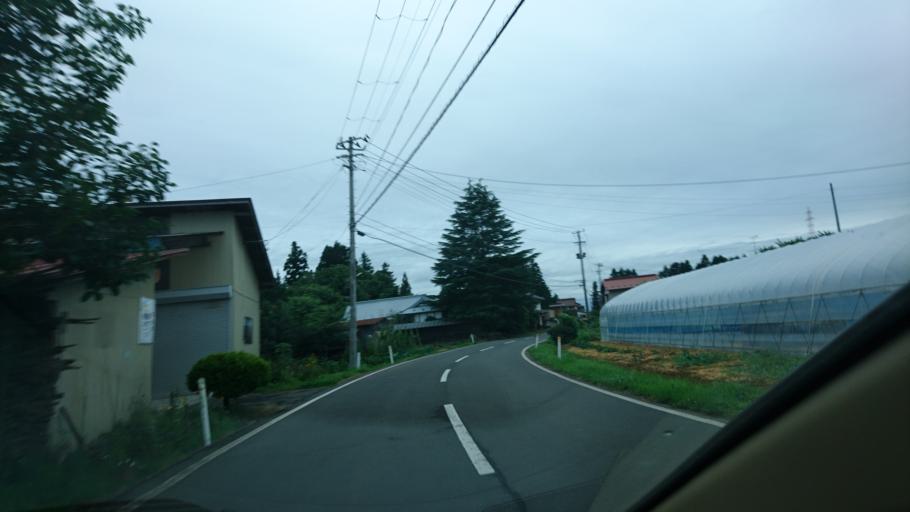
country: JP
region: Iwate
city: Mizusawa
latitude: 39.0738
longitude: 141.1832
